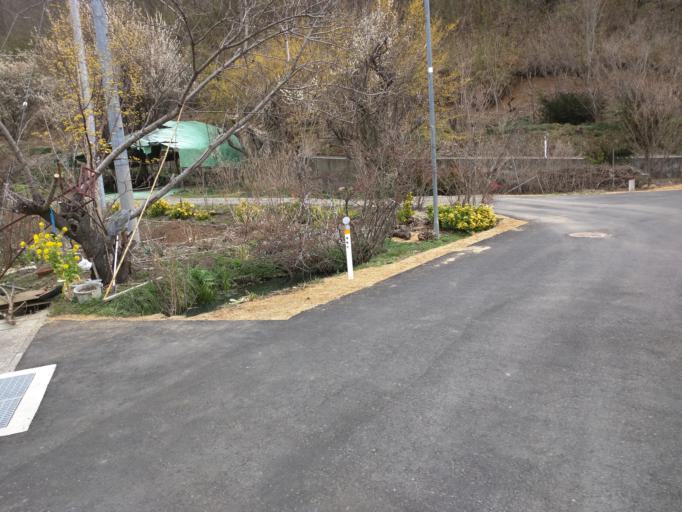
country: JP
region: Fukushima
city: Fukushima-shi
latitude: 37.7427
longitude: 140.4943
